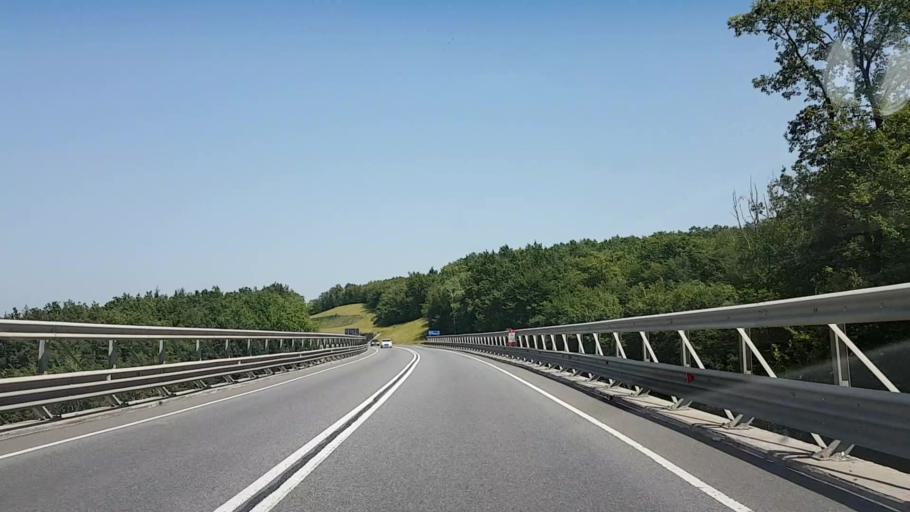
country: RO
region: Cluj
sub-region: Comuna Feleacu
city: Gheorghieni
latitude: 46.7281
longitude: 23.6662
